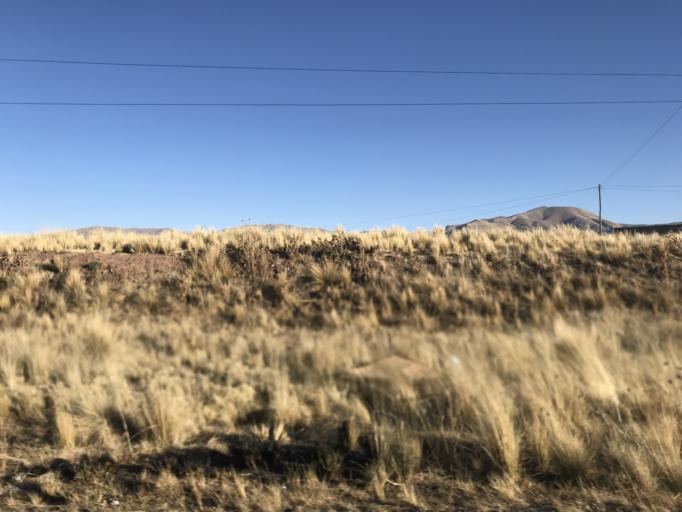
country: BO
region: La Paz
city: Tiahuanaco
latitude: -16.5684
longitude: -68.6571
